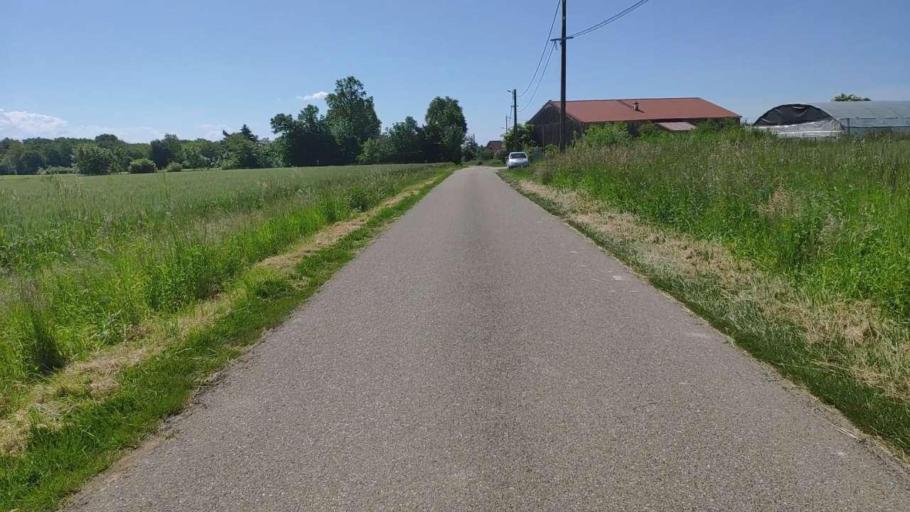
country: FR
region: Franche-Comte
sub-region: Departement du Jura
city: Bletterans
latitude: 46.7685
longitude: 5.4084
